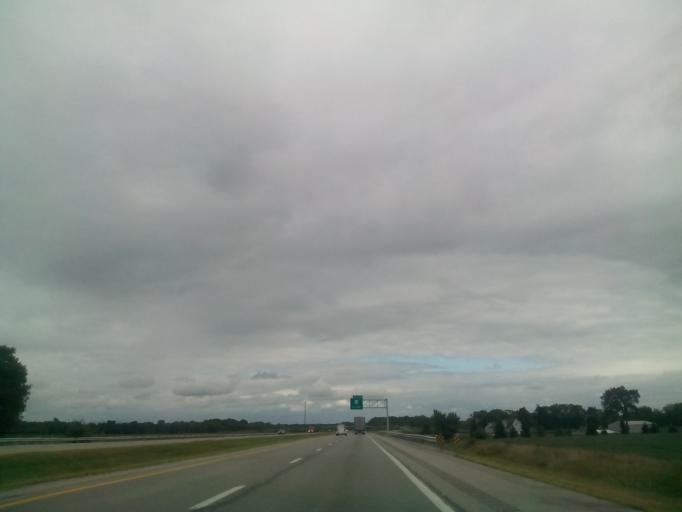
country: US
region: Ohio
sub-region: Fulton County
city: Burlington
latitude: 41.5939
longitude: -84.3606
